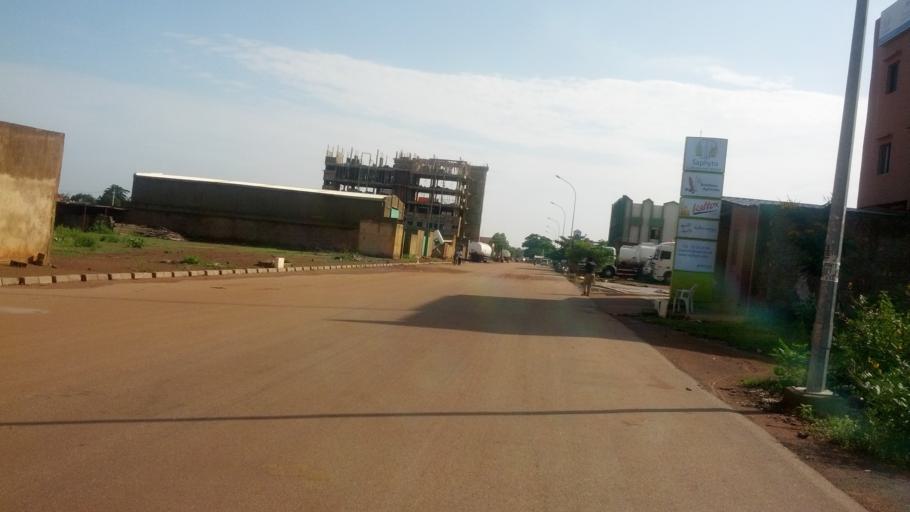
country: BF
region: Centre
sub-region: Kadiogo Province
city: Ouagadougou
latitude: 12.3509
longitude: -1.4930
